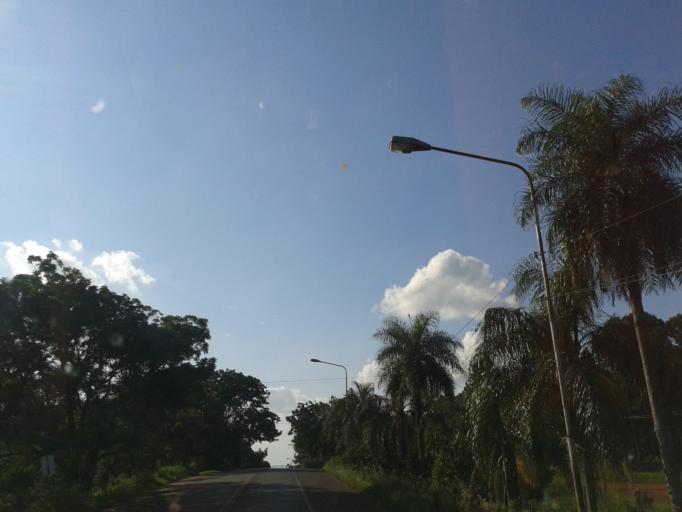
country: AR
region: Misiones
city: Guarani
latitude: -27.4937
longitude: -55.1702
